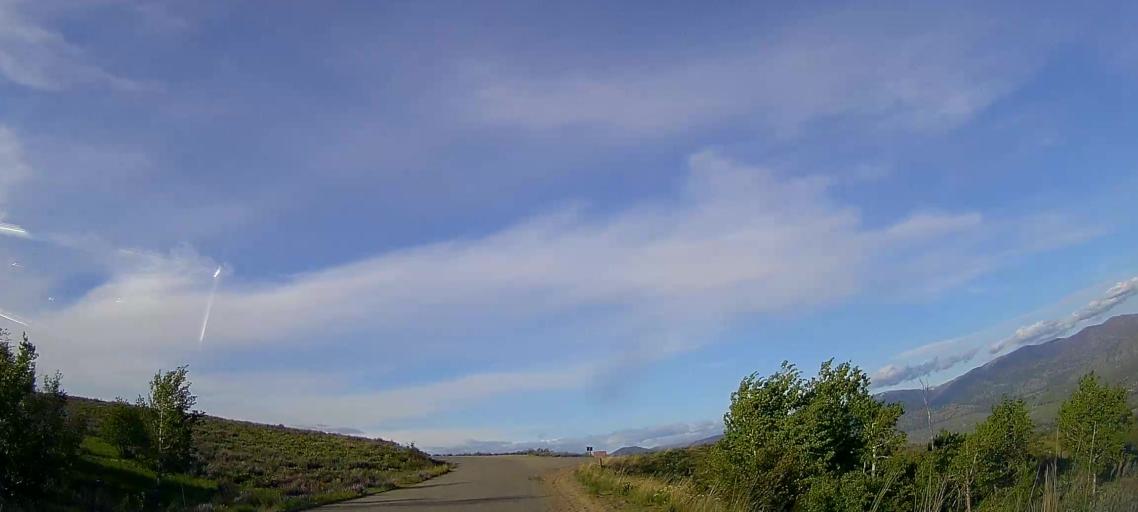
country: US
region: Washington
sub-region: Chelan County
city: Granite Falls
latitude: 48.4731
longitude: -120.2538
